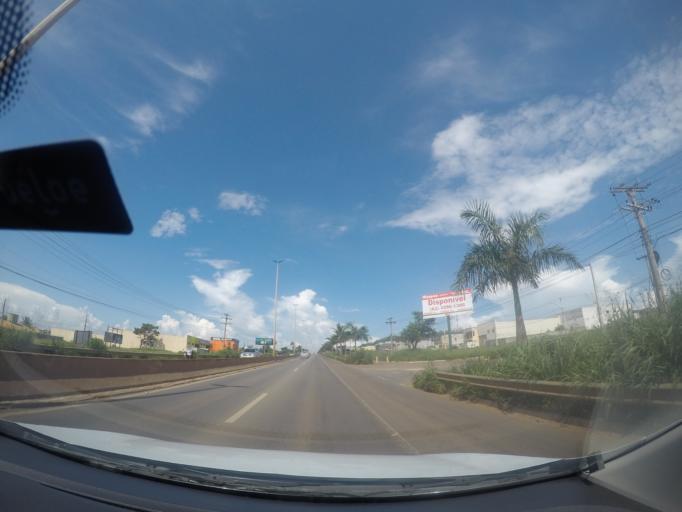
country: BR
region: Goias
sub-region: Goiania
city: Goiania
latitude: -16.6596
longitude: -49.3544
